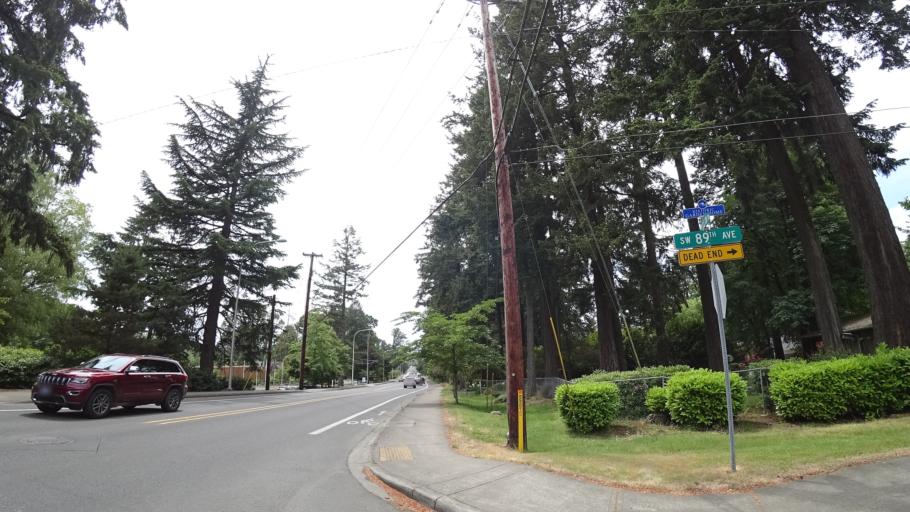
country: US
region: Oregon
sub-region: Washington County
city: Garden Home-Whitford
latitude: 45.4570
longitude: -122.7670
